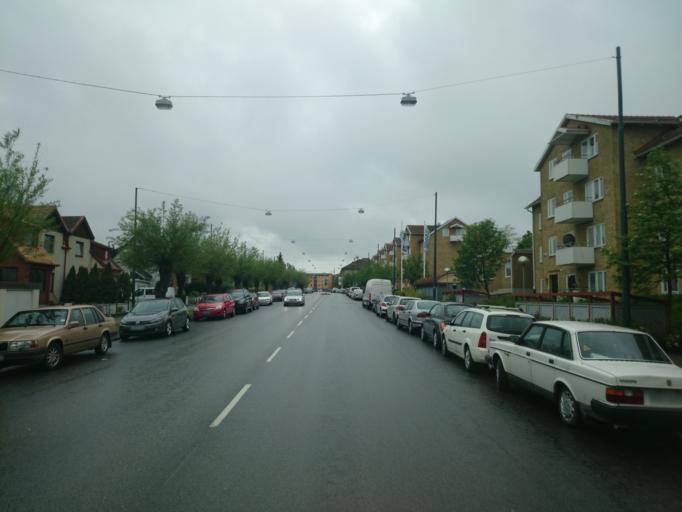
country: SE
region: Skane
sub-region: Malmo
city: Malmoe
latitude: 55.5822
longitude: 13.0333
